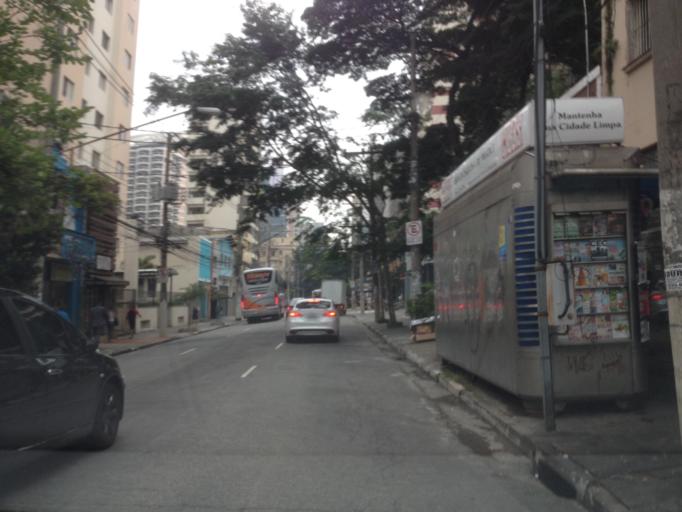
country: BR
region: Sao Paulo
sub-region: Sao Paulo
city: Sao Paulo
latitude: -23.5825
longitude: -46.6741
